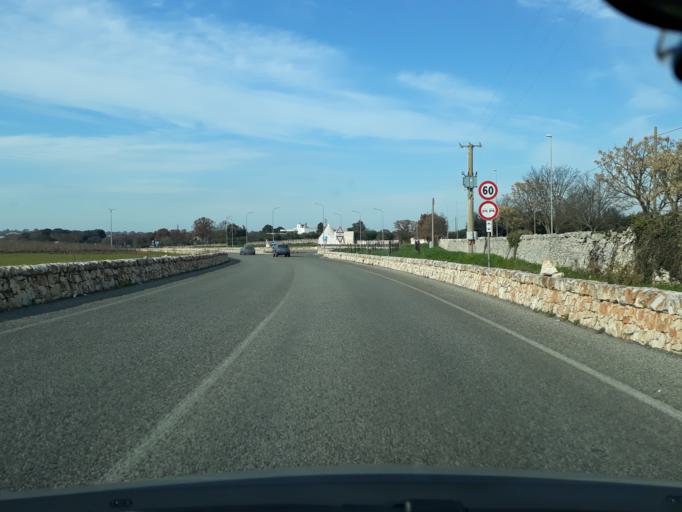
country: IT
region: Apulia
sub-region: Provincia di Bari
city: Locorotondo
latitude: 40.7566
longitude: 17.3431
